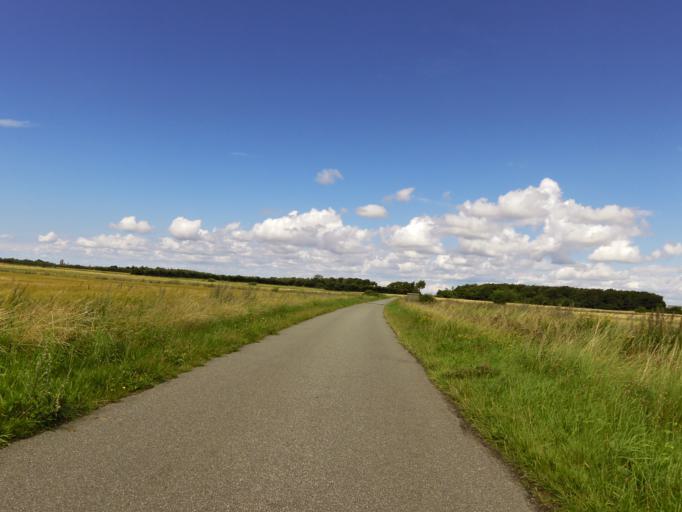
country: DK
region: South Denmark
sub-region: Esbjerg Kommune
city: Ribe
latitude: 55.3058
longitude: 8.7911
